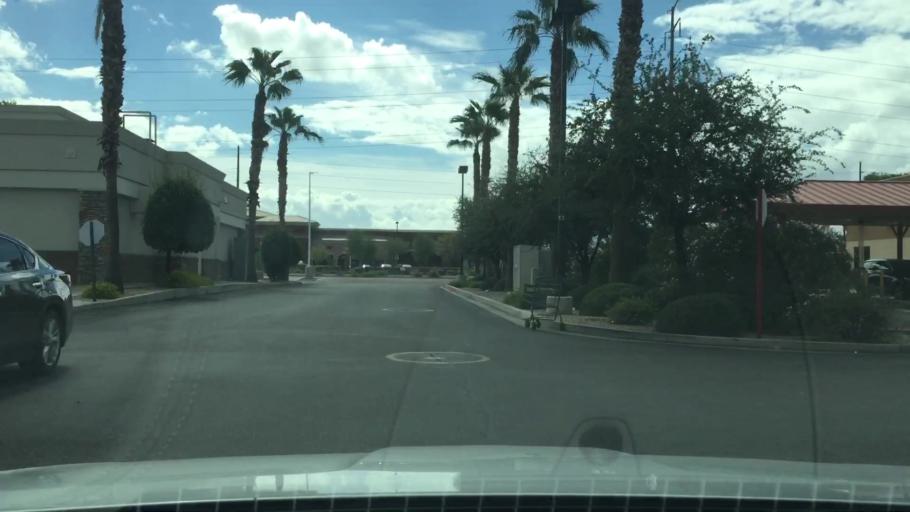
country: US
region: Arizona
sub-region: Maricopa County
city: Laveen
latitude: 33.3785
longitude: -112.1692
